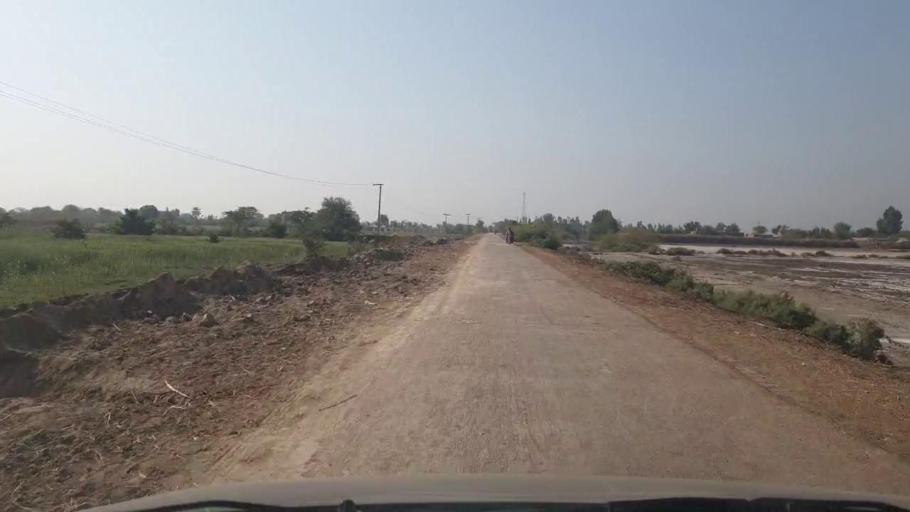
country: PK
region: Sindh
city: Mirwah Gorchani
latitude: 25.3043
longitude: 69.1495
